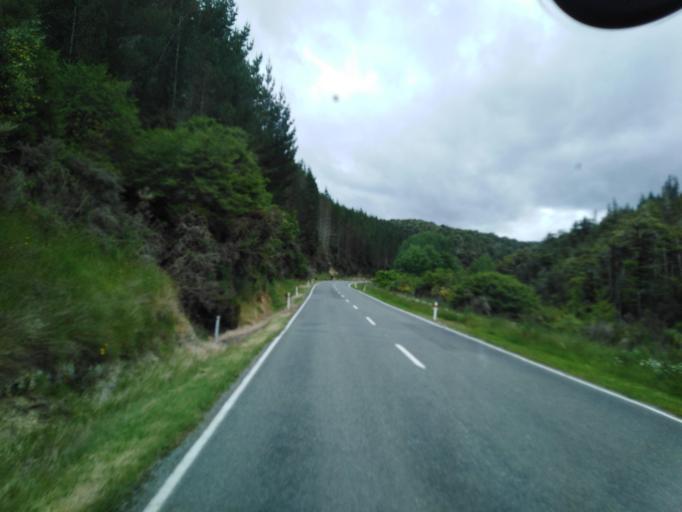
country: NZ
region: Tasman
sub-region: Tasman District
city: Wakefield
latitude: -41.6245
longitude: 172.7374
